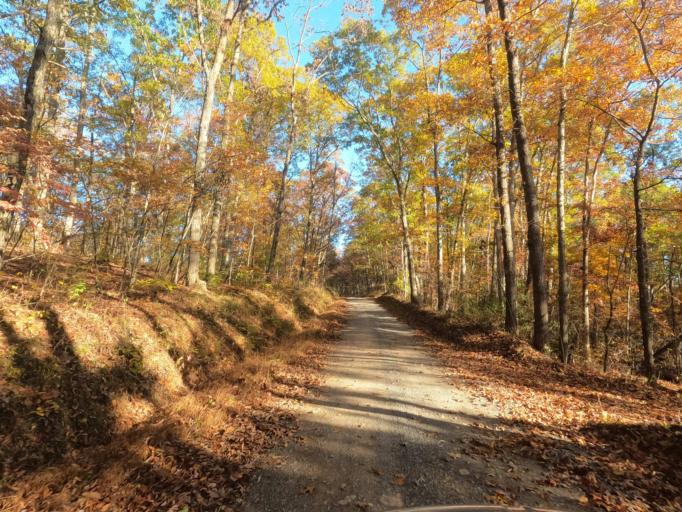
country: US
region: West Virginia
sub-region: Mineral County
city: Fort Ashby
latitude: 39.5335
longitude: -78.5361
